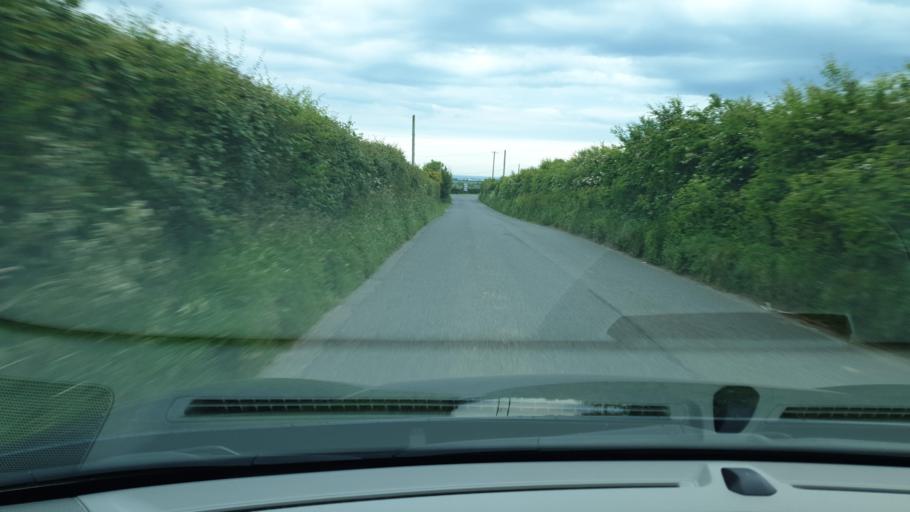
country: IE
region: Leinster
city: Lusk
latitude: 53.5544
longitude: -6.1560
